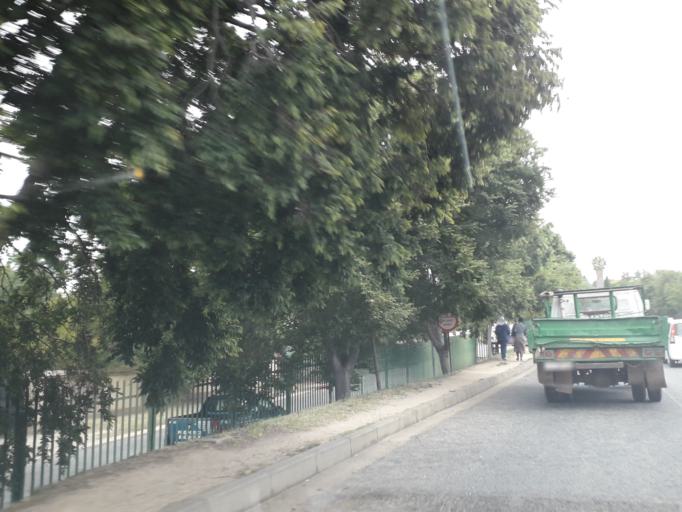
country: ZA
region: Gauteng
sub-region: City of Johannesburg Metropolitan Municipality
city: Roodepoort
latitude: -26.1048
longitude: 27.9462
